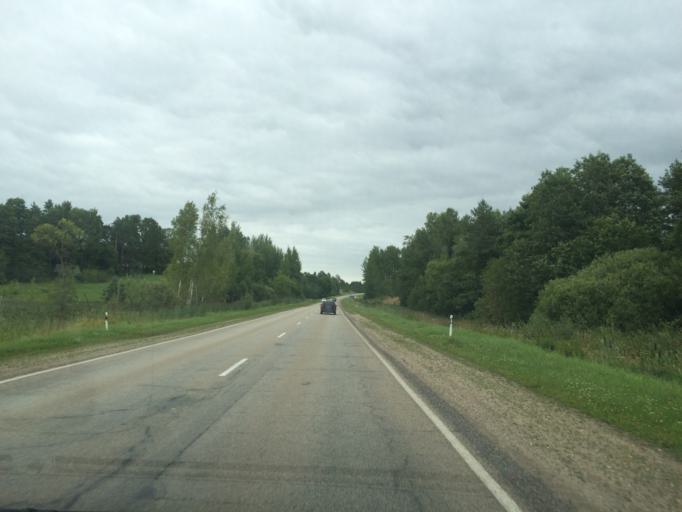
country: LV
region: Rezekne
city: Rezekne
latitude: 56.5747
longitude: 27.3767
